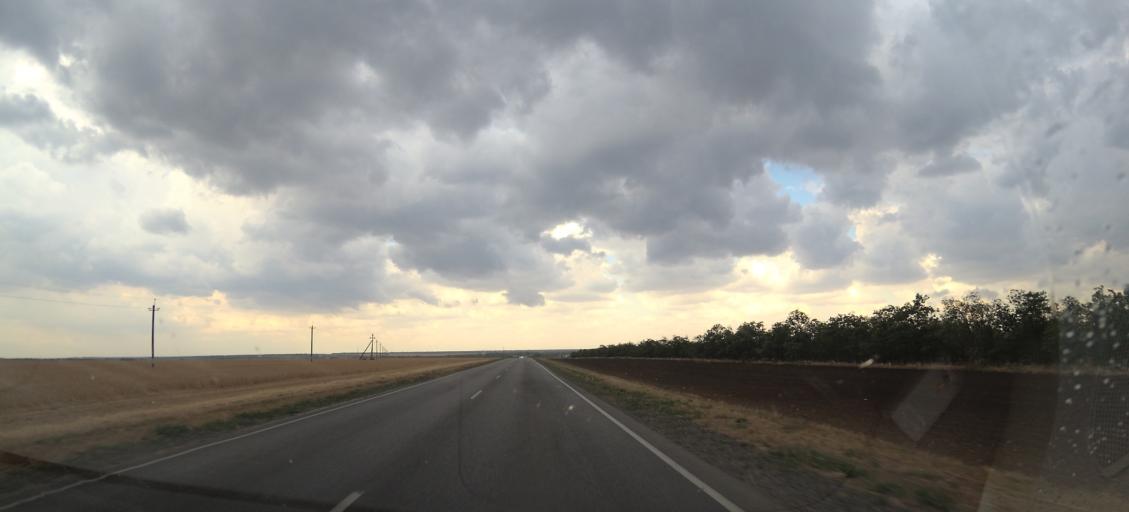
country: RU
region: Rostov
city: Orlovskiy
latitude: 46.8805
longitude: 42.0148
